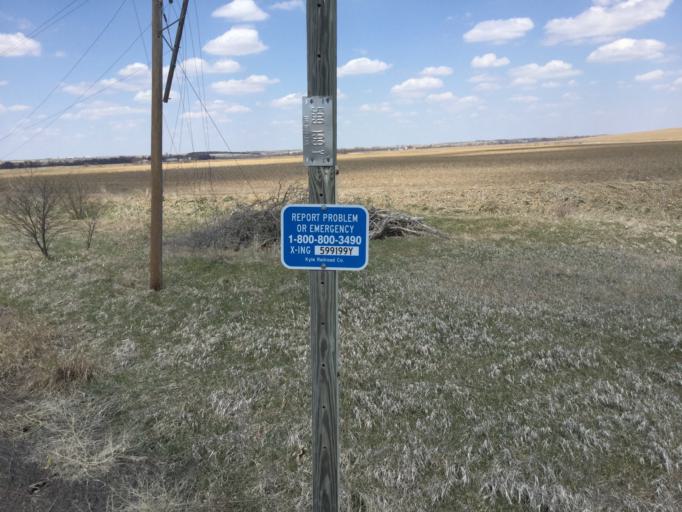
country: US
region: Kansas
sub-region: Norton County
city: Norton
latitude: 39.8859
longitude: -99.6715
